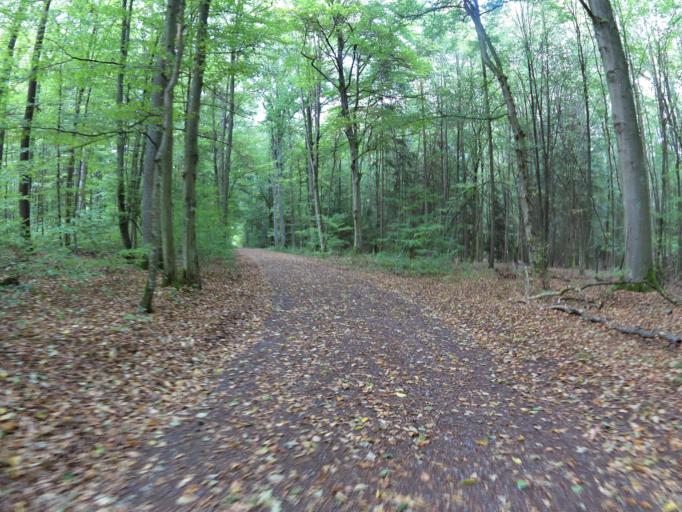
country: DE
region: Bavaria
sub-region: Regierungsbezirk Unterfranken
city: Waldbrunn
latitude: 49.7735
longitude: 9.8068
